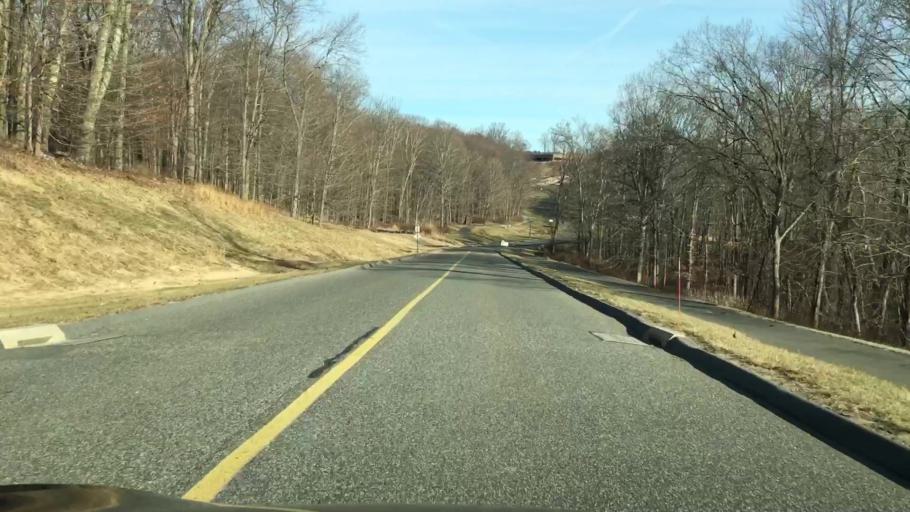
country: US
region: Connecticut
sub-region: Fairfield County
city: Danbury
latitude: 41.3748
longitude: -73.5117
